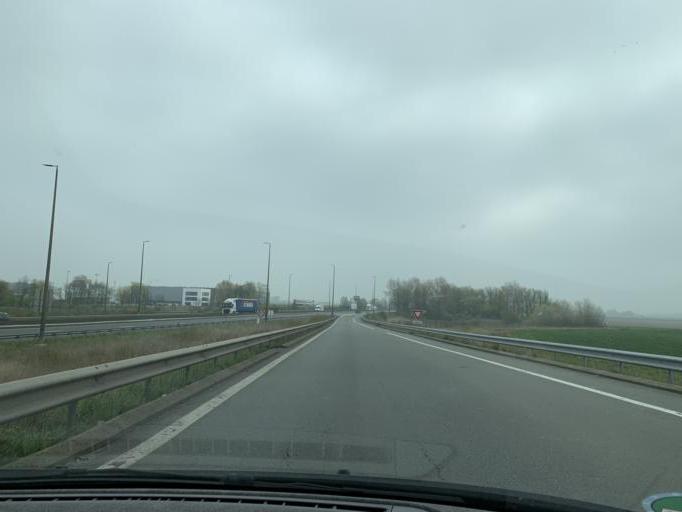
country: FR
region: Nord-Pas-de-Calais
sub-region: Departement du Pas-de-Calais
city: Marck
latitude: 50.9372
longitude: 1.9419
